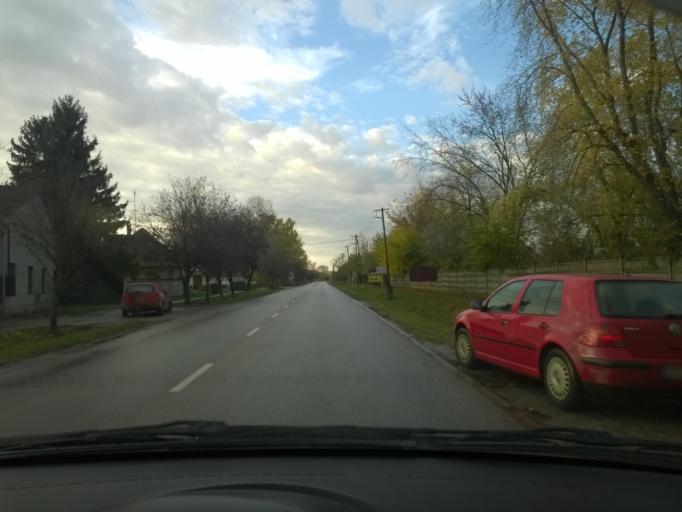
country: HU
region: Bacs-Kiskun
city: Kalocsa
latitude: 46.5192
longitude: 18.9907
